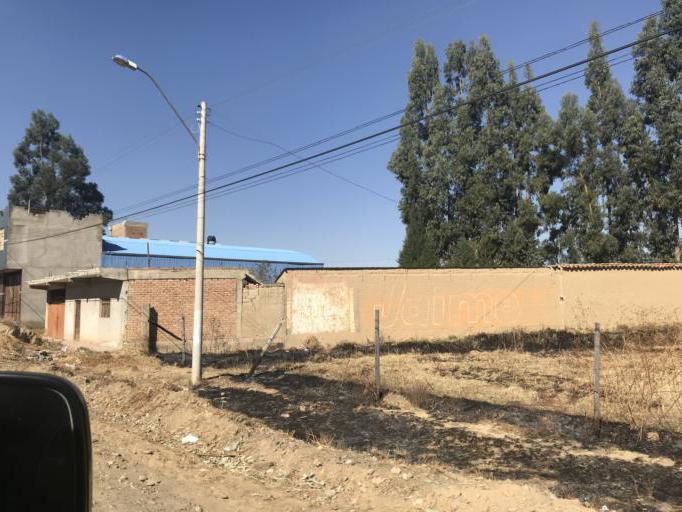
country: BO
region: Cochabamba
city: Punata
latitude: -17.5580
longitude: -65.8649
